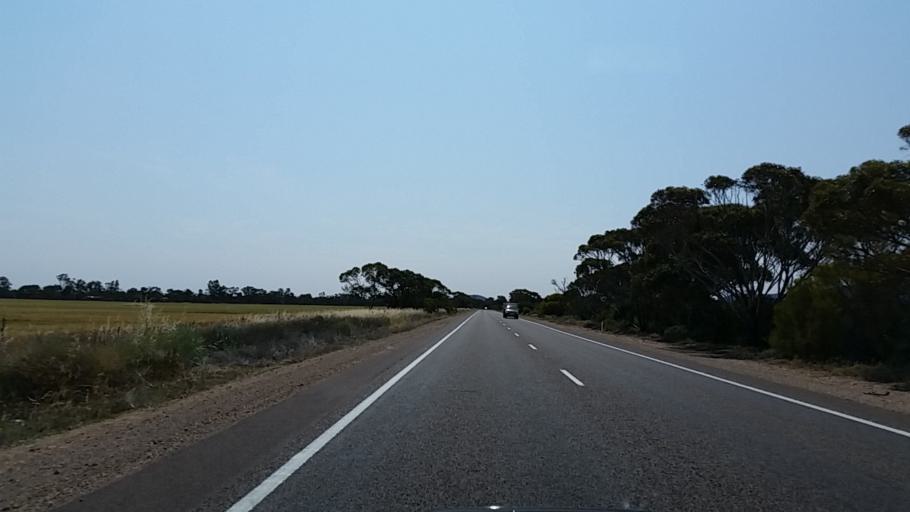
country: AU
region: South Australia
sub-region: Port Pirie City and Dists
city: Port Pirie
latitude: -32.8644
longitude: 137.9822
